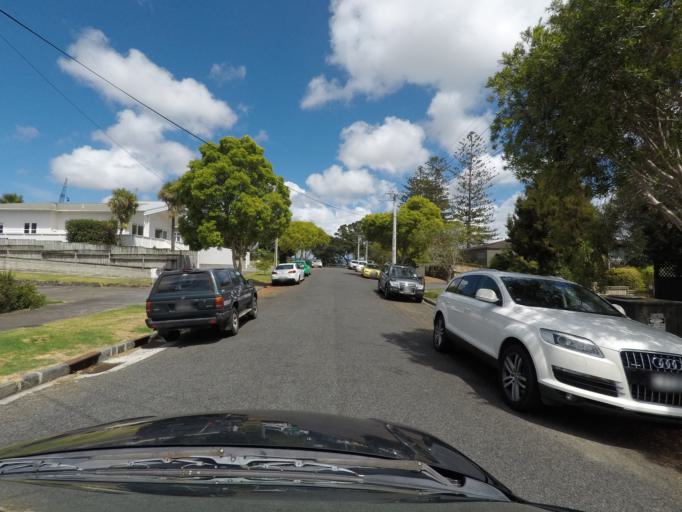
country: NZ
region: Auckland
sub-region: Auckland
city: Rosebank
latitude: -36.8615
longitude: 174.7003
